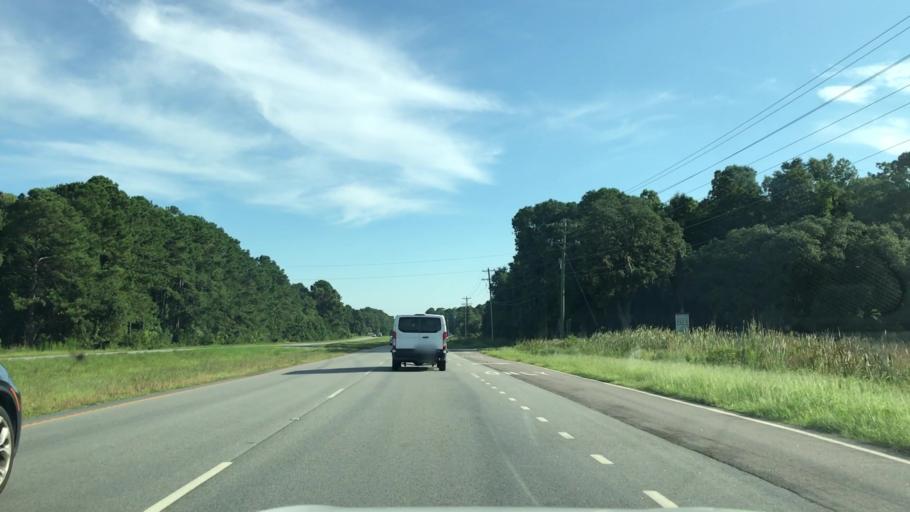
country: US
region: South Carolina
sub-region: Charleston County
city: Awendaw
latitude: 32.9212
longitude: -79.7156
